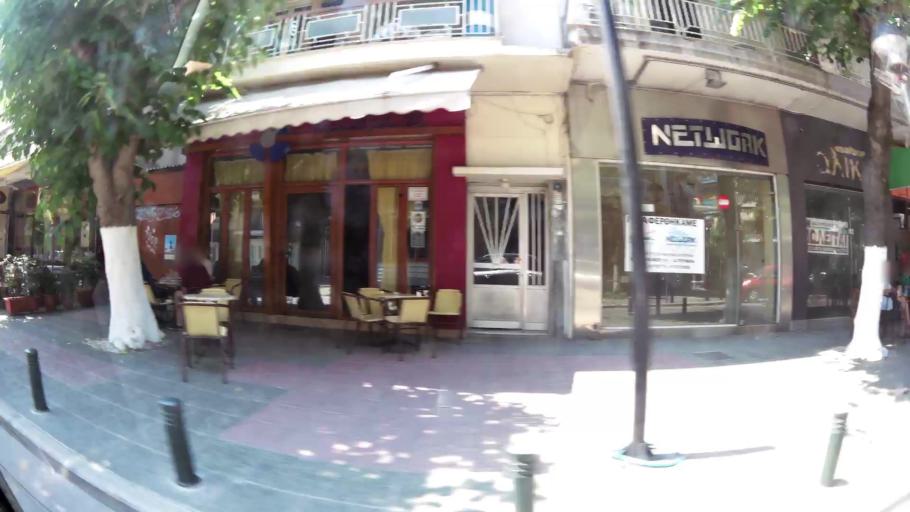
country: GR
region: Central Macedonia
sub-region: Nomos Thessalonikis
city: Ampelokipoi
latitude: 40.6495
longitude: 22.9225
